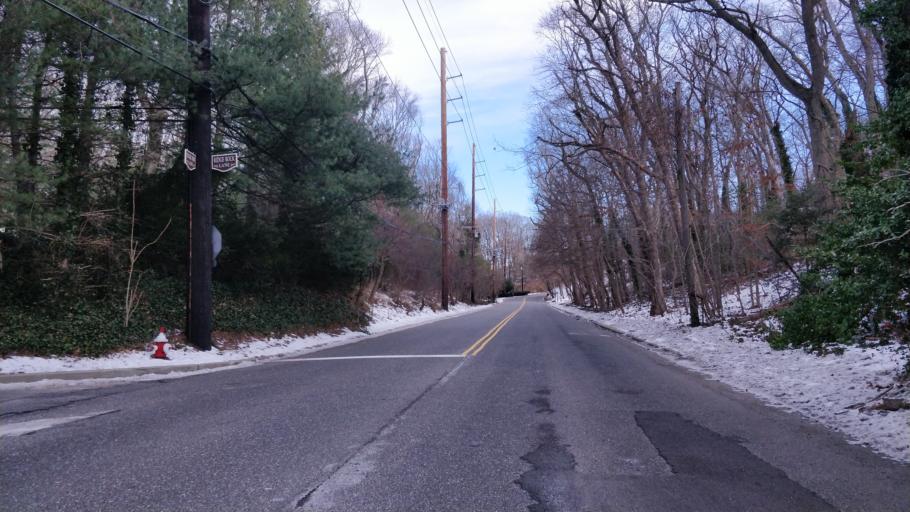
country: US
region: New York
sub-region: Nassau County
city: East Norwich
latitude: 40.8456
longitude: -73.5266
